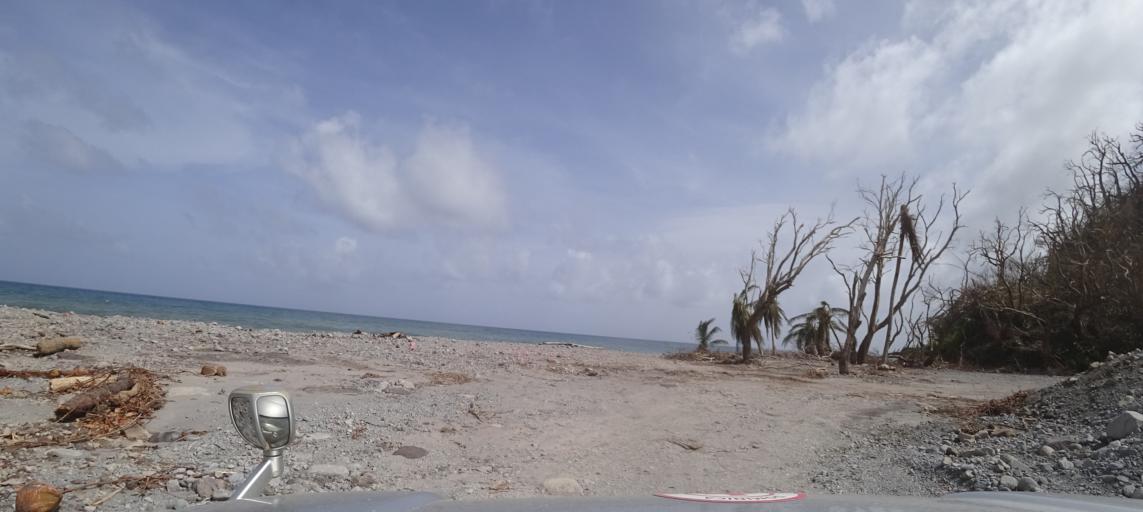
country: DM
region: Saint Patrick
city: La Plaine
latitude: 15.3208
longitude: -61.2445
